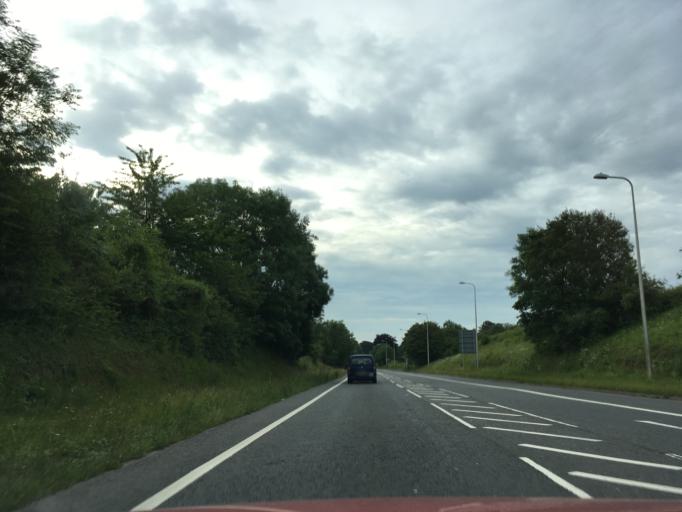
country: GB
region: England
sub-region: North Somerset
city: Easton-in-Gordano
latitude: 51.4743
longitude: -2.7038
